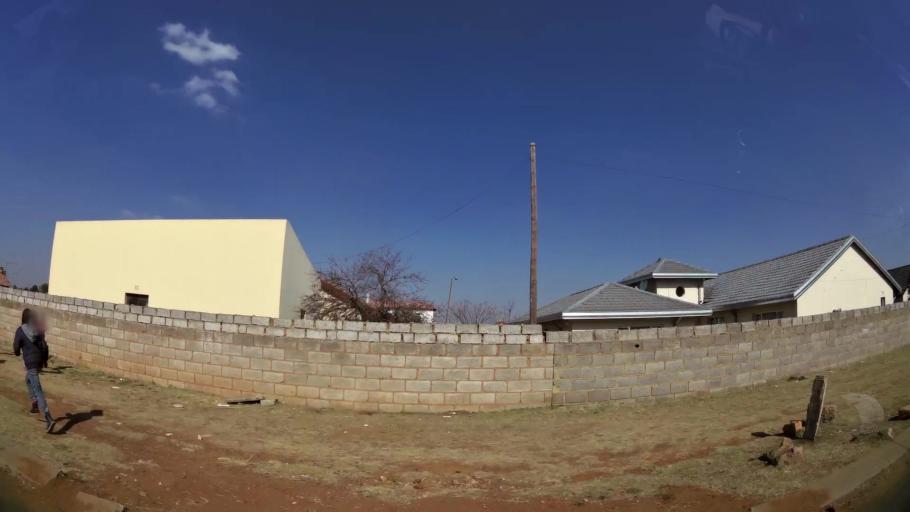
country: ZA
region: Gauteng
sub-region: City of Johannesburg Metropolitan Municipality
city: Roodepoort
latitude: -26.1701
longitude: 27.8007
